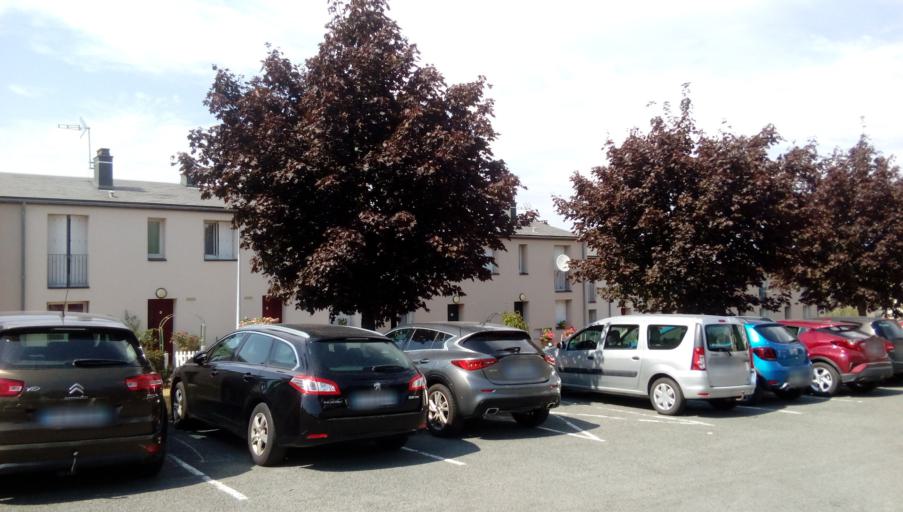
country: FR
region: Limousin
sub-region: Departement de la Creuse
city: Gueret
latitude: 46.1760
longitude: 1.8776
